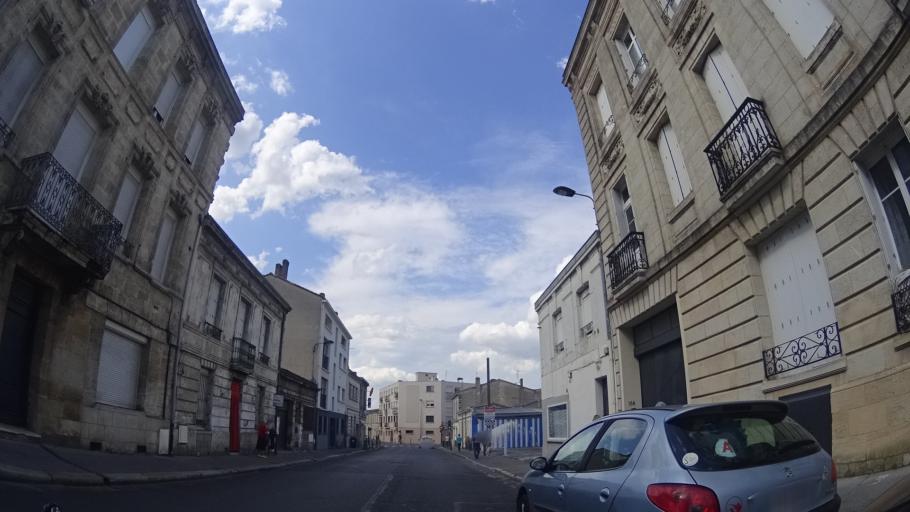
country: FR
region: Aquitaine
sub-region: Departement de la Gironde
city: Bordeaux
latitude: 44.8230
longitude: -0.5658
